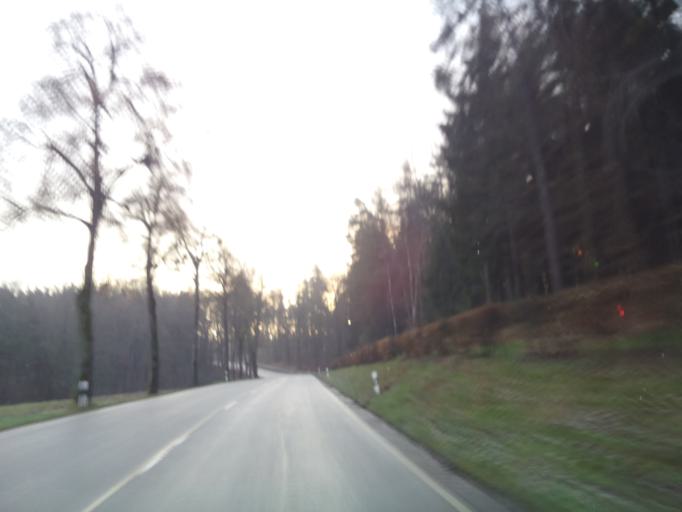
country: DE
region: Bavaria
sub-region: Upper Franconia
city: Lichtenfels
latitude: 50.1727
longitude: 11.0281
